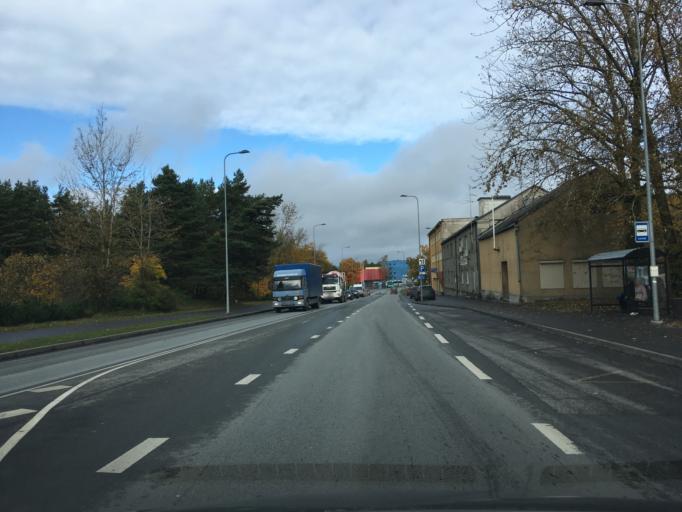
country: EE
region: Harju
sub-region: Tallinna linn
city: Tallinn
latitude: 59.3694
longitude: 24.7175
